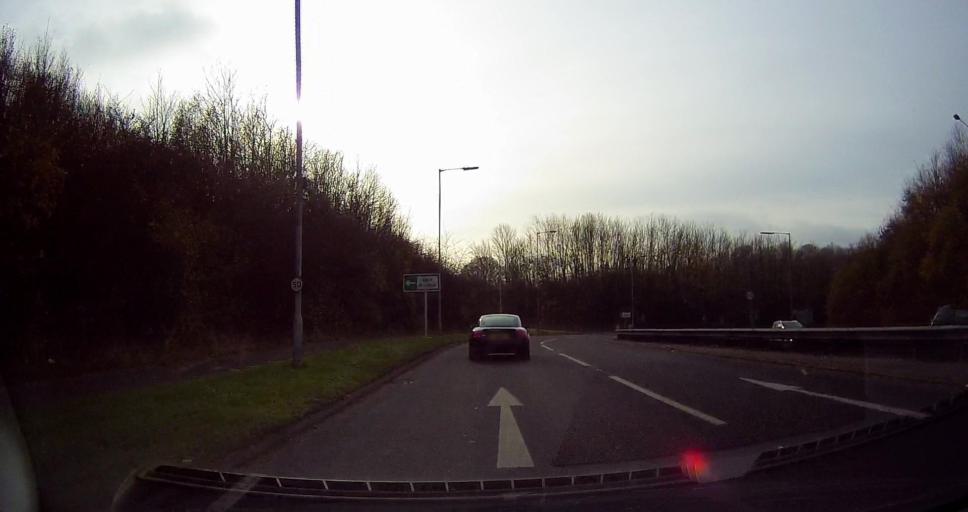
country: GB
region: England
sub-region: Brighton and Hove
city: Hove
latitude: 50.8684
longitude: -0.1519
